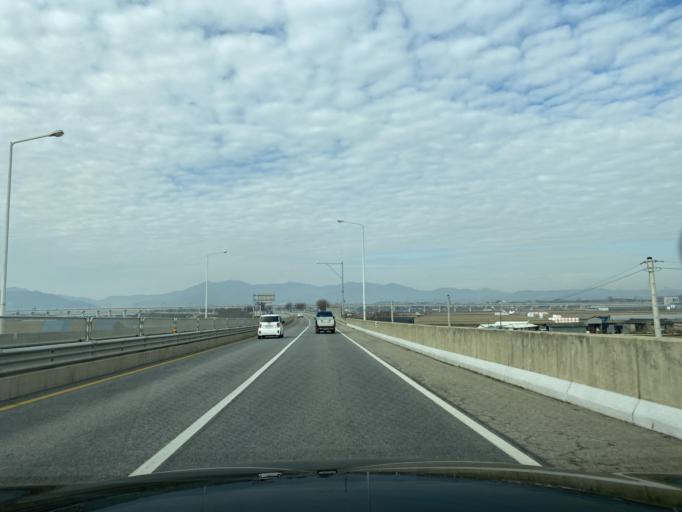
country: KR
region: Chungcheongnam-do
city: Yesan
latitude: 36.6919
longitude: 126.7351
